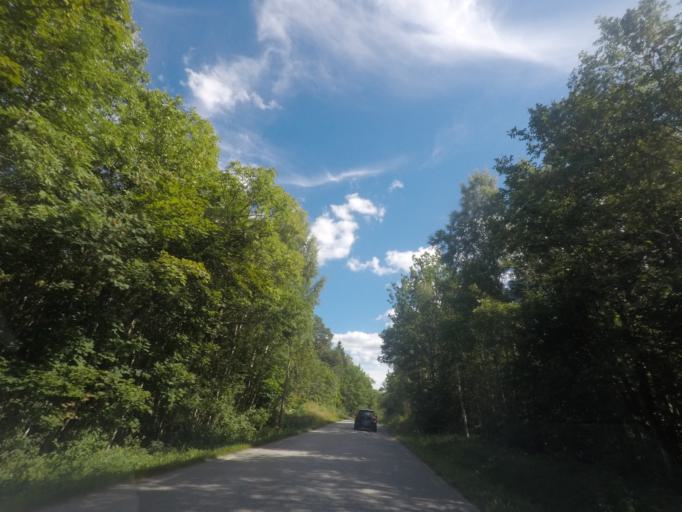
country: SE
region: Stockholm
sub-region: Norrtalje Kommun
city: Arno
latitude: 60.1178
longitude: 18.7910
